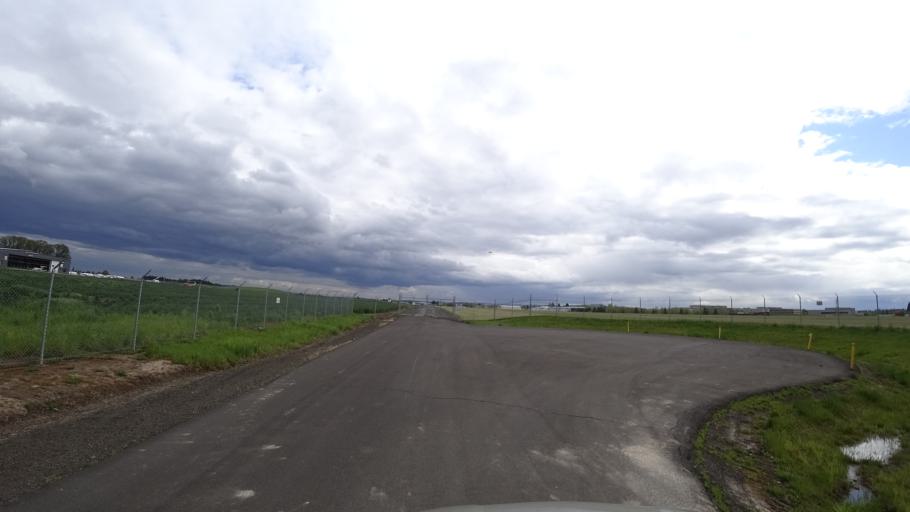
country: US
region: Oregon
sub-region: Washington County
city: Hillsboro
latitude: 45.5500
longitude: -122.9528
